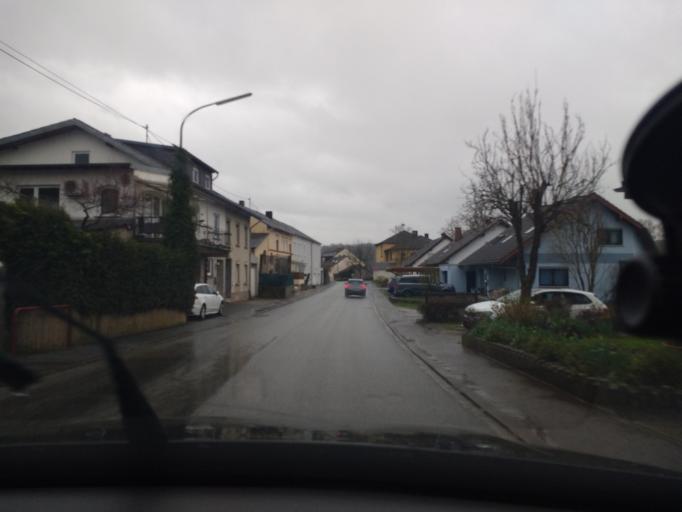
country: DE
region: Rheinland-Pfalz
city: Wawern
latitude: 49.6551
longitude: 6.5454
